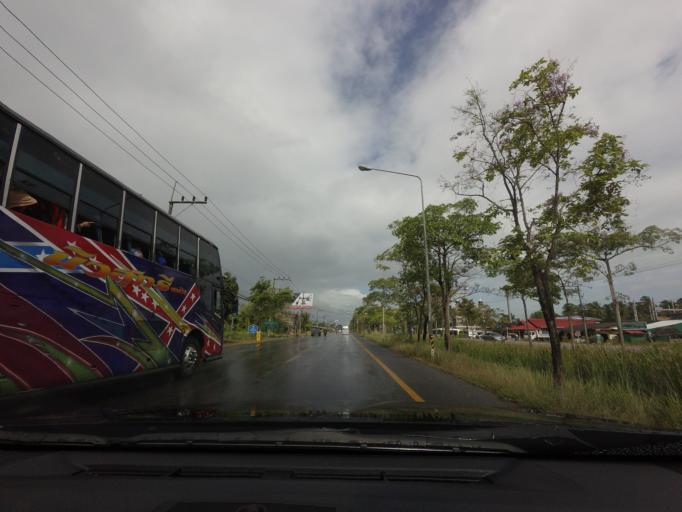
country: TH
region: Pattani
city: Nong Chik
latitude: 6.8039
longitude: 101.1385
